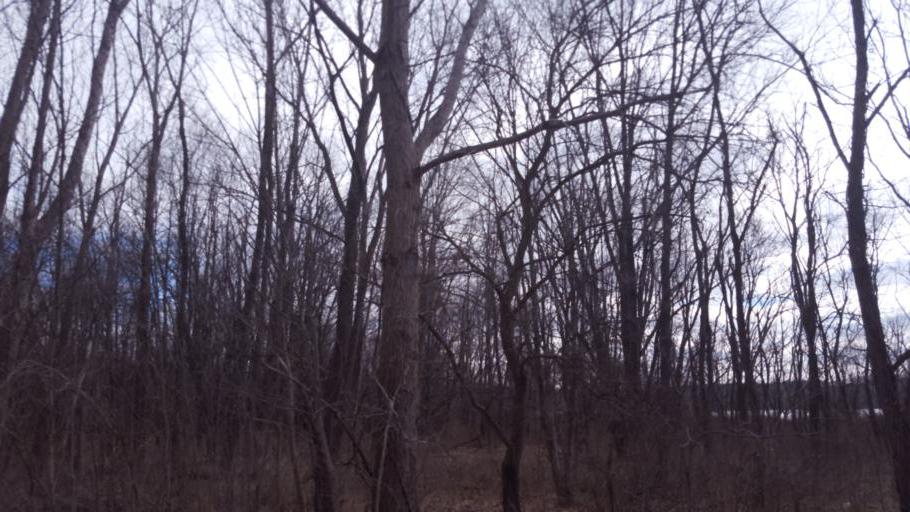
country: US
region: Ohio
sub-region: Knox County
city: Fredericktown
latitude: 40.5158
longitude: -82.5023
